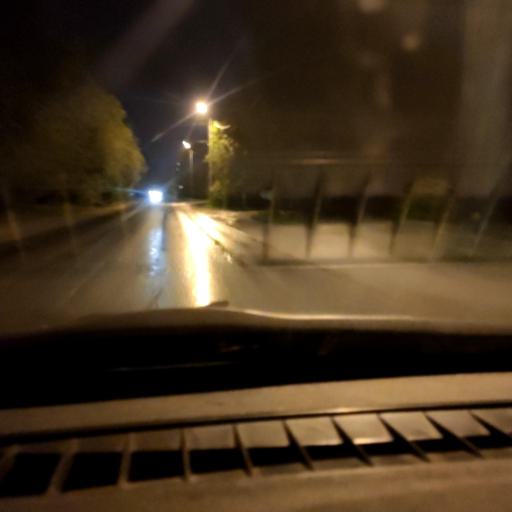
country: RU
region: Samara
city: Syzran'
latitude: 53.1724
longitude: 48.5181
